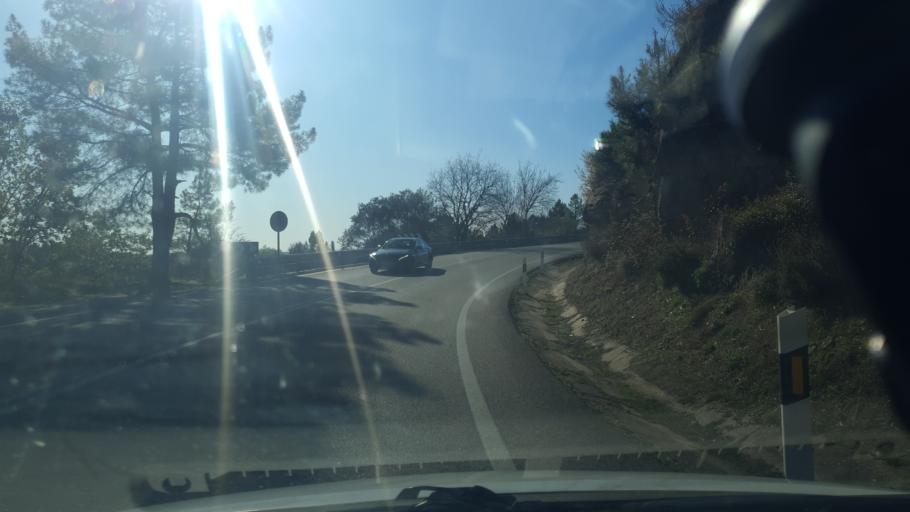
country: ES
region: Castille and Leon
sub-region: Provincia de Avila
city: Arenas de San Pedro
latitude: 40.1980
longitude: -5.0451
